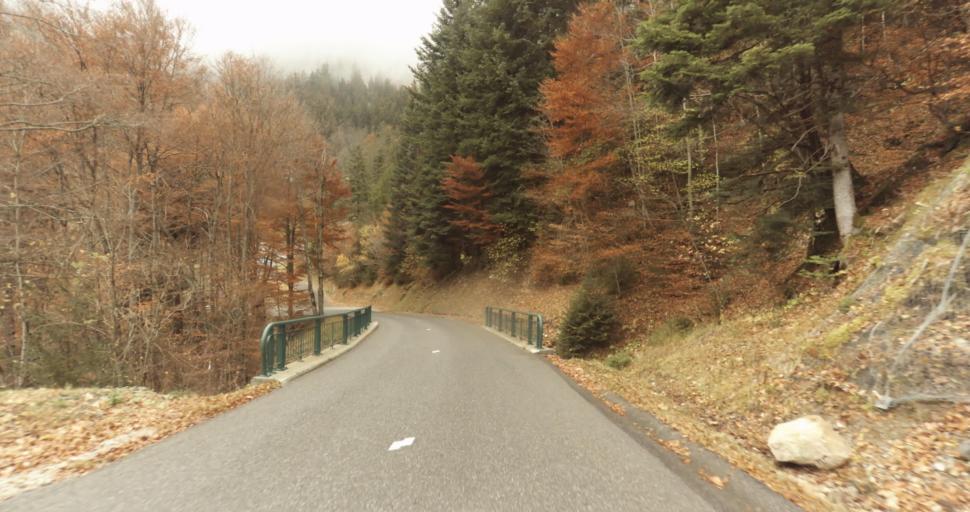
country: FR
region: Rhone-Alpes
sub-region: Departement de la Haute-Savoie
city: Thorens-Glieres
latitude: 45.9684
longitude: 6.2985
